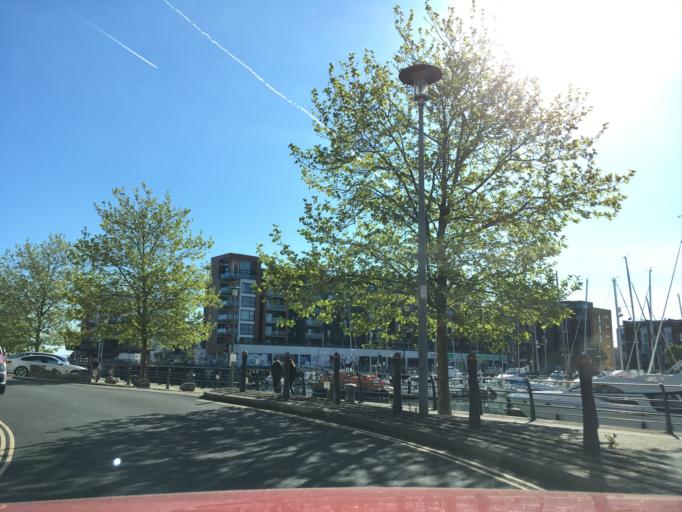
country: GB
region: England
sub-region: North Somerset
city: Portishead
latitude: 51.4910
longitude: -2.7595
